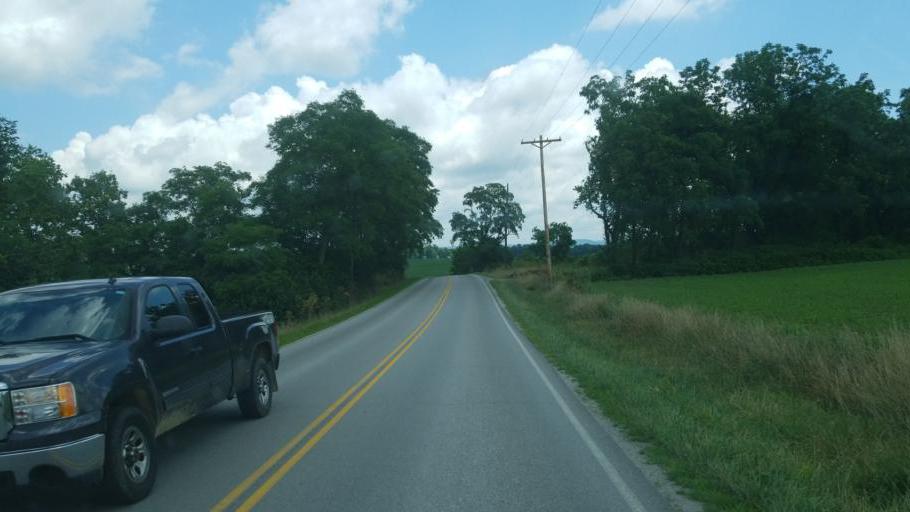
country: US
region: Ohio
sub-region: Highland County
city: Leesburg
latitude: 39.2691
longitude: -83.4730
